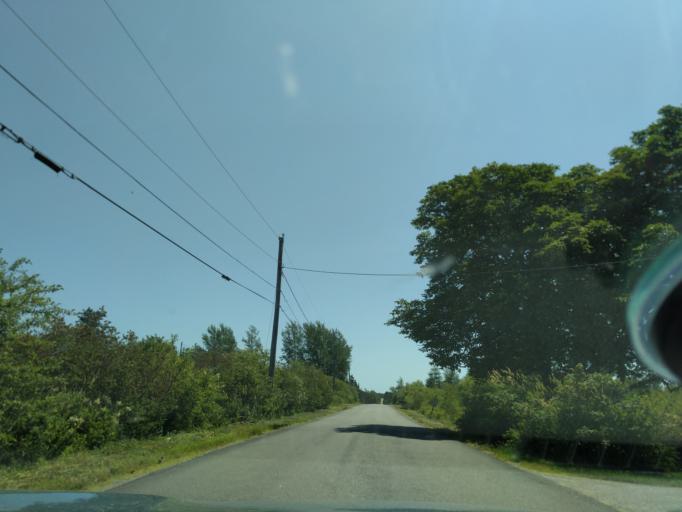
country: US
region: Maine
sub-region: Washington County
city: Eastport
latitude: 44.8403
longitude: -67.0147
